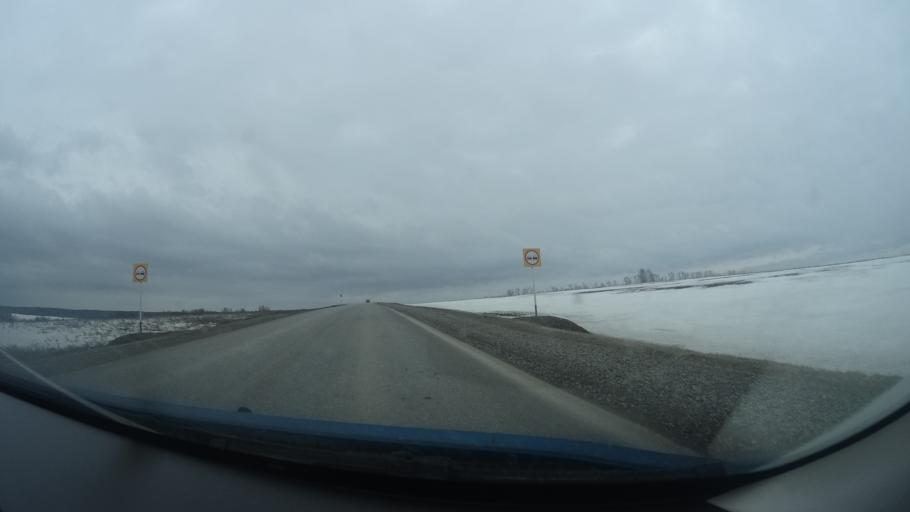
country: RU
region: Bashkortostan
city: Birsk
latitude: 55.3534
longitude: 55.5844
